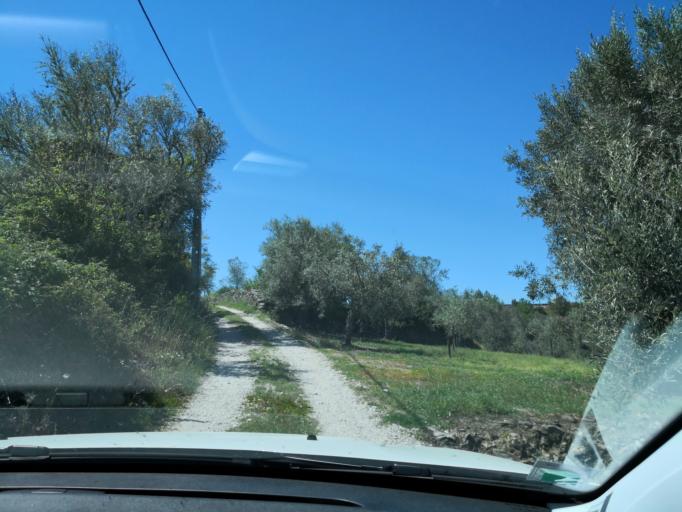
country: PT
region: Vila Real
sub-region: Vila Real
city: Vila Real
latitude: 41.2420
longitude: -7.7212
